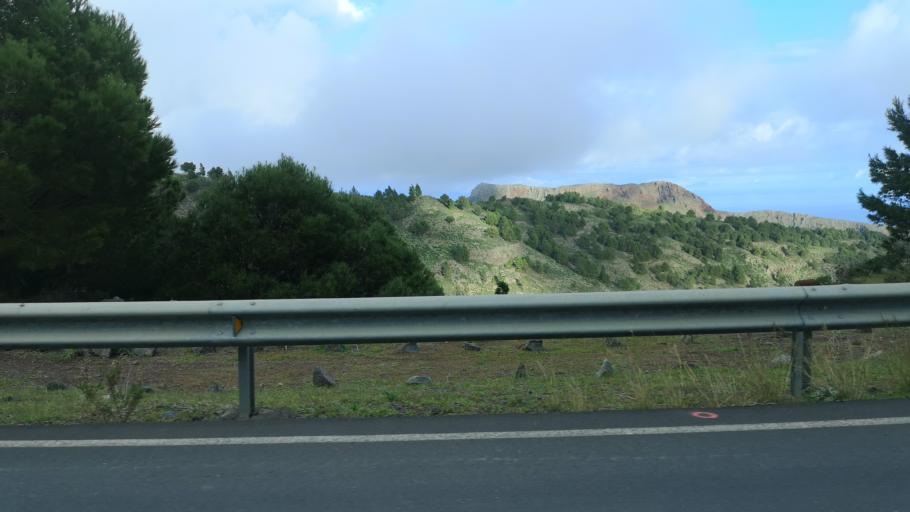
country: ES
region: Canary Islands
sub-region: Provincia de Santa Cruz de Tenerife
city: Alajero
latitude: 28.0840
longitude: -17.2001
